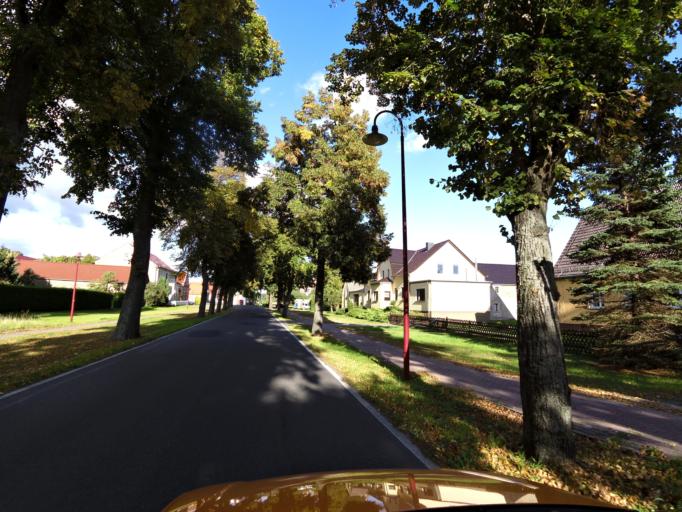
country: DE
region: Brandenburg
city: Trebbin
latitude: 52.1618
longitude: 13.1851
